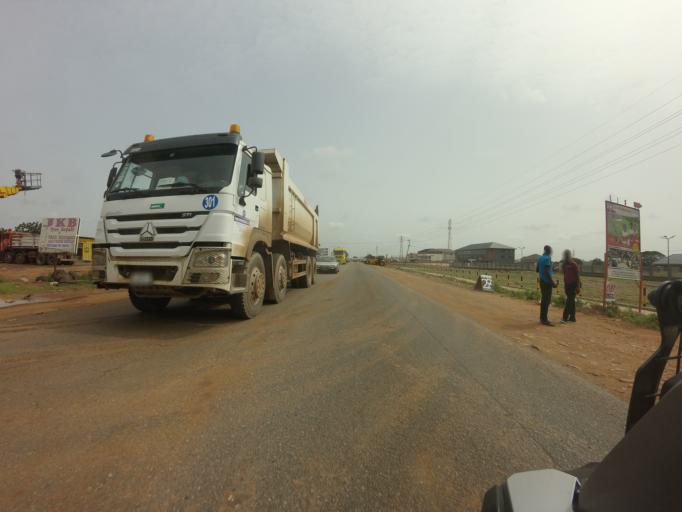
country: GH
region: Greater Accra
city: Tema
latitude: 5.7301
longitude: 0.0263
